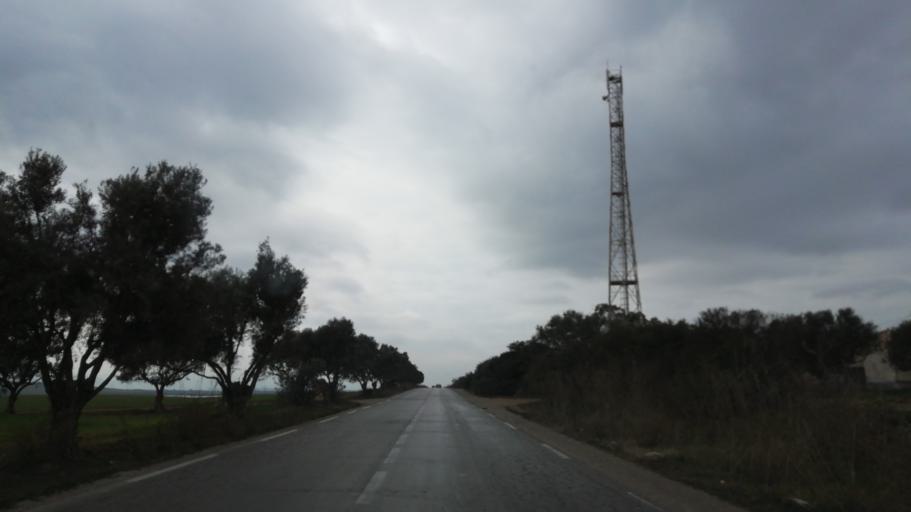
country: DZ
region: Oran
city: Sidi ech Chahmi
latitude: 35.6118
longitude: -0.4249
